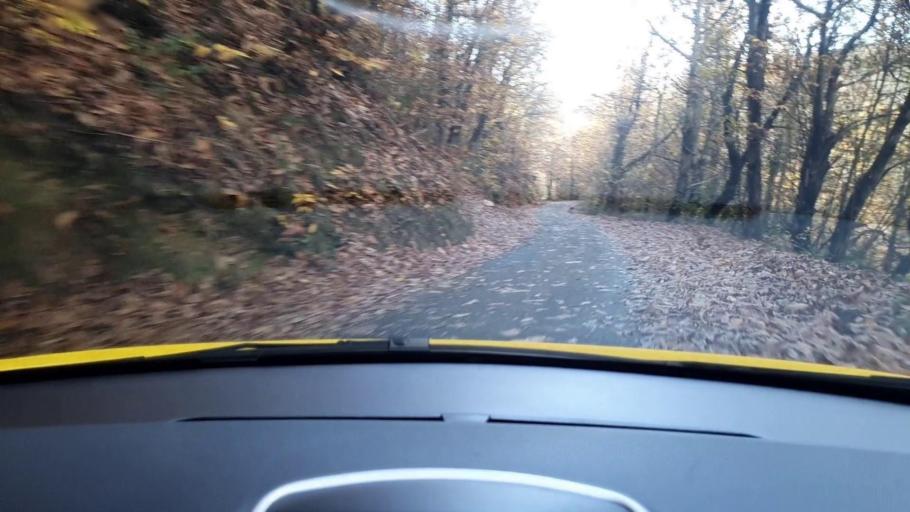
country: FR
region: Languedoc-Roussillon
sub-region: Departement du Gard
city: Valleraugue
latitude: 44.0983
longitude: 3.7389
